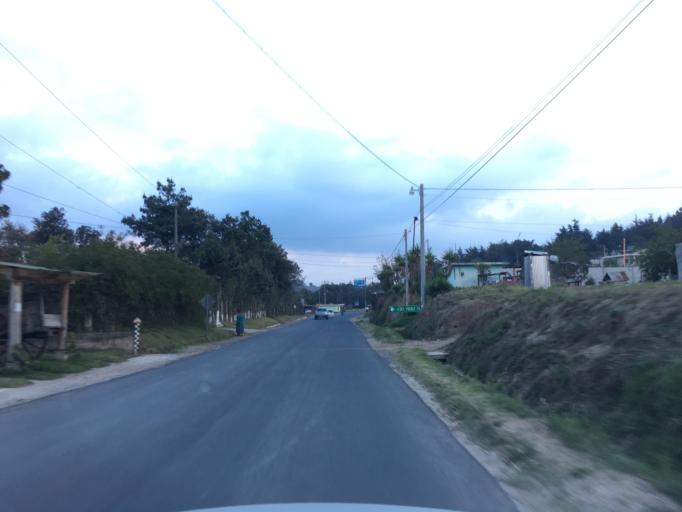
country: GT
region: Chimaltenango
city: Tecpan Guatemala
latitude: 14.7477
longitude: -91.0001
